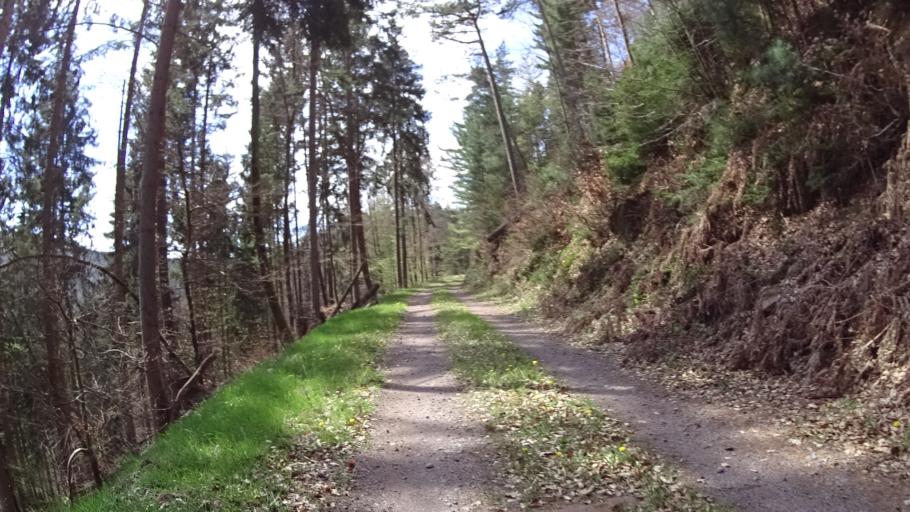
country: DE
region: Rheinland-Pfalz
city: Ramberg
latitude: 49.3215
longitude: 7.9959
